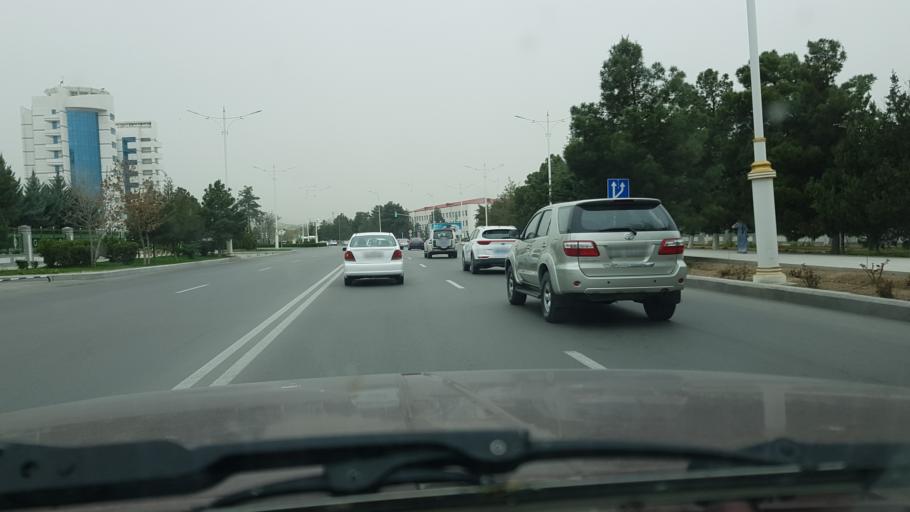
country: TM
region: Ahal
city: Ashgabat
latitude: 37.9514
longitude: 58.3414
